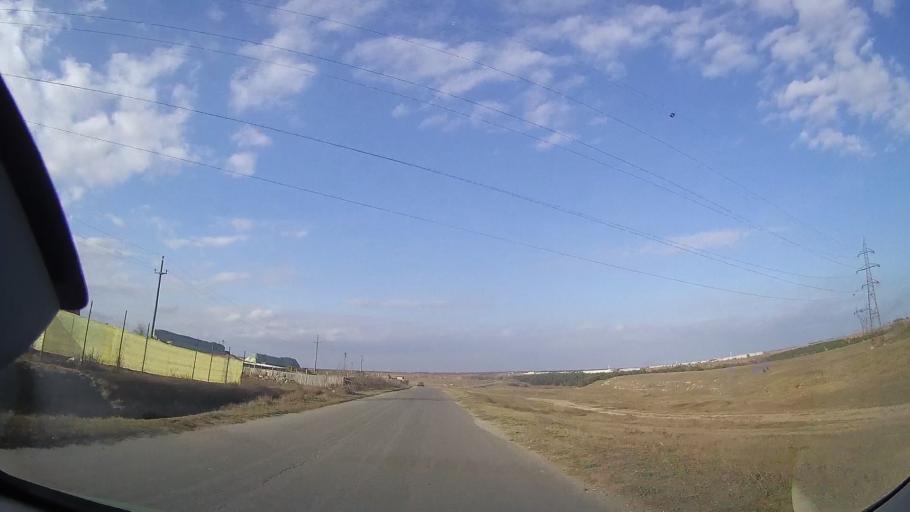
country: RO
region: Constanta
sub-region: Comuna Limanu
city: Limanu
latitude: 43.8029
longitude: 28.5215
